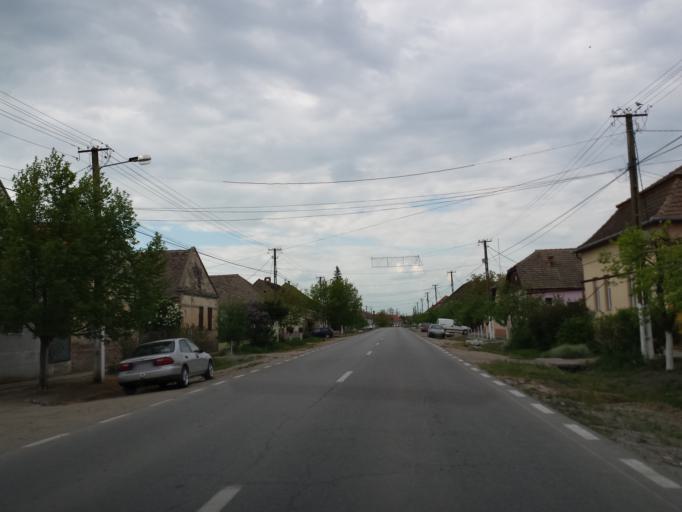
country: RO
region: Timis
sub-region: Comuna Cenad
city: Cenad
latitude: 46.1294
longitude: 20.5910
